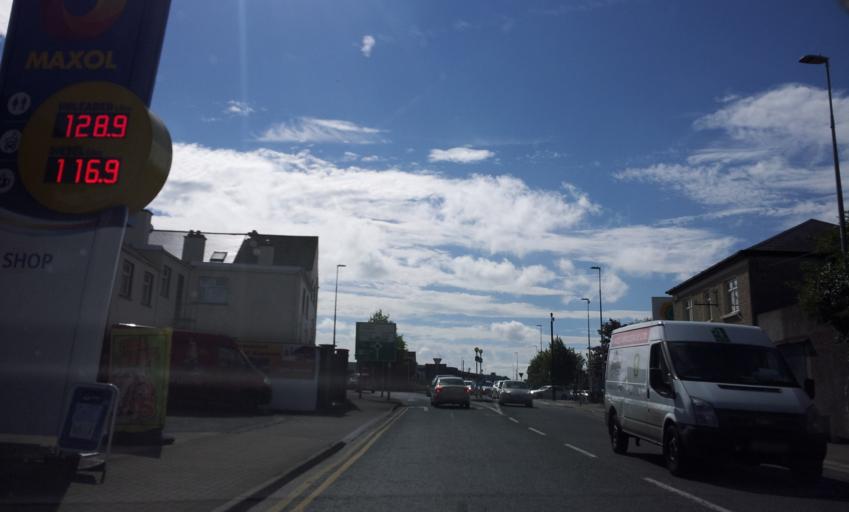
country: IE
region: Leinster
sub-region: Laois
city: Portlaoise
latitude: 53.0333
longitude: -7.3025
